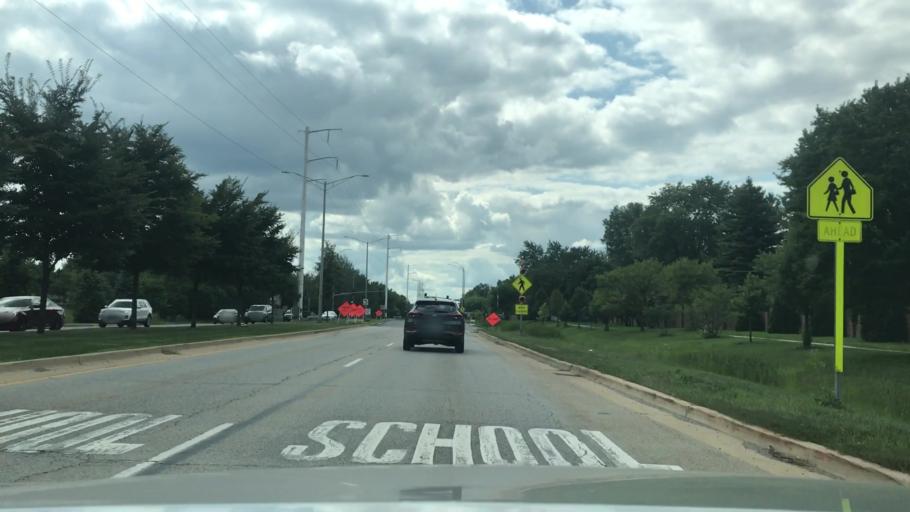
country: US
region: Illinois
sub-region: DuPage County
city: Naperville
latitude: 41.7483
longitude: -88.1368
